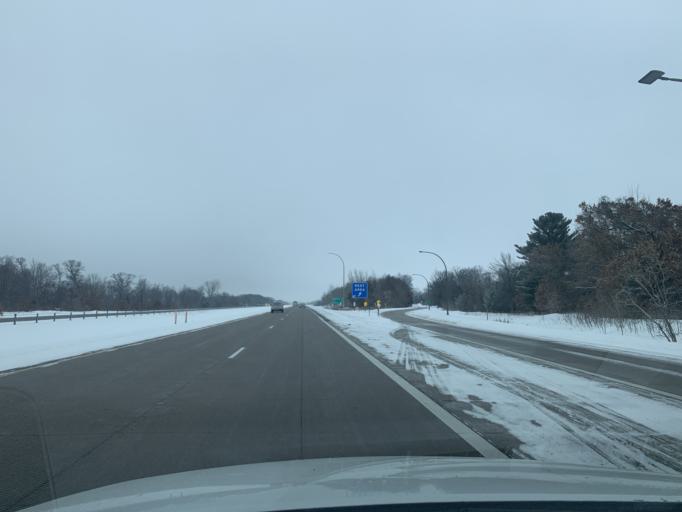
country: US
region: Minnesota
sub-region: Chisago County
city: Harris
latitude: 45.5951
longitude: -92.9957
